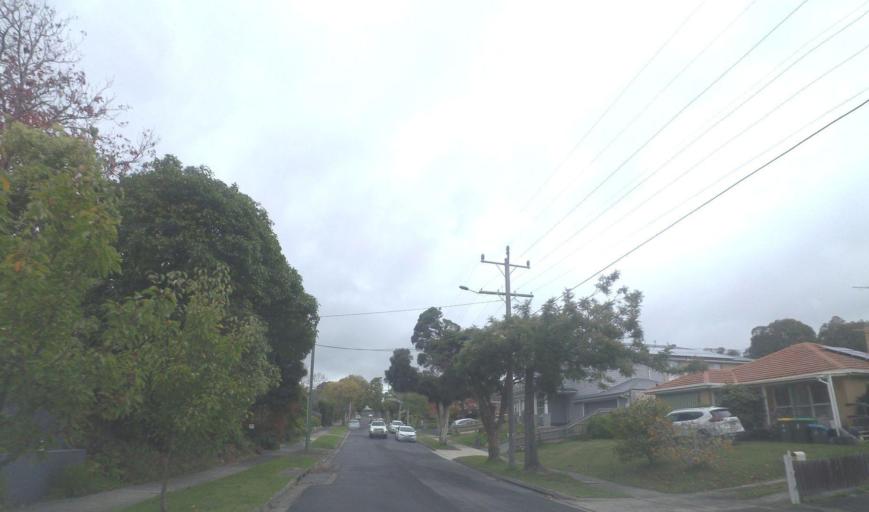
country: AU
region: Victoria
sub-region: Whitehorse
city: Blackburn North
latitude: -37.8046
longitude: 145.1633
